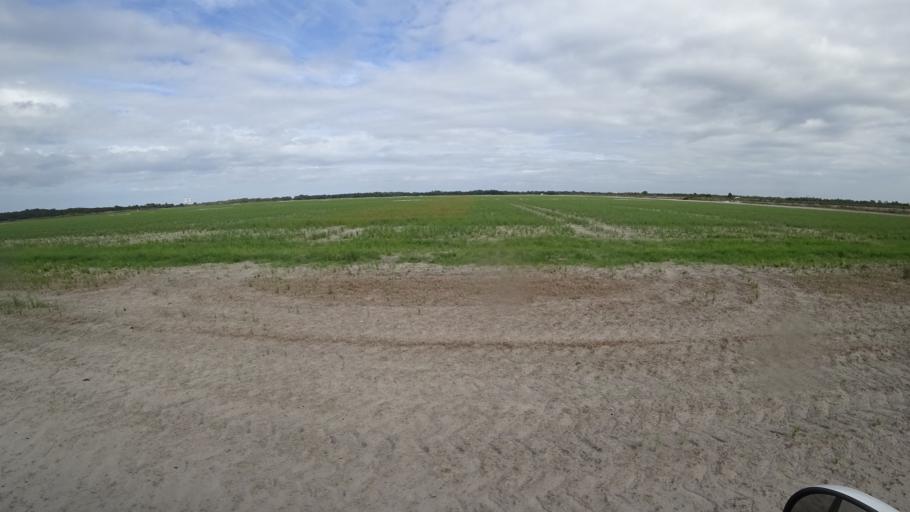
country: US
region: Florida
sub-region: Hillsborough County
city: Wimauma
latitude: 27.5590
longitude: -82.3034
